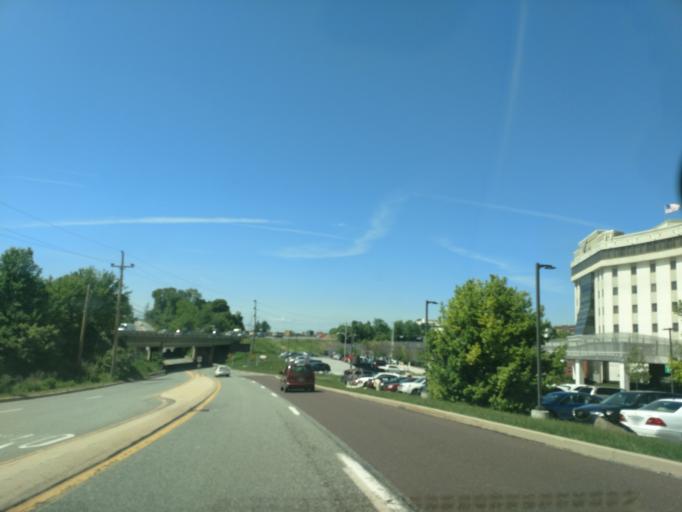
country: US
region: Pennsylvania
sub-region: Montgomery County
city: King of Prussia
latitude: 40.0962
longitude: -75.4174
